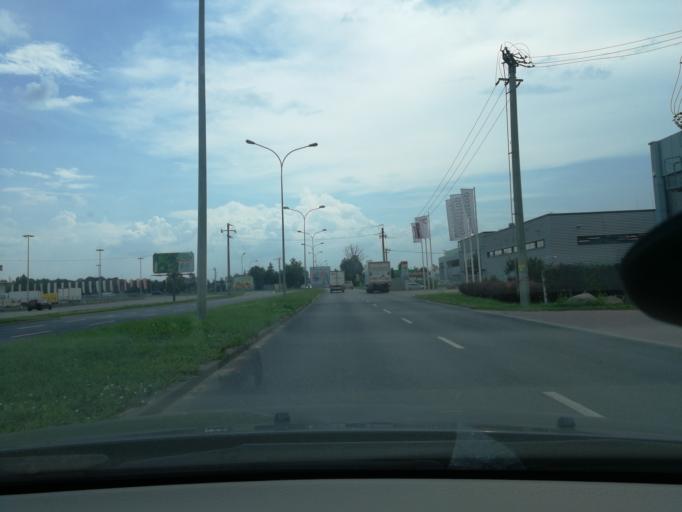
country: PL
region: Masovian Voivodeship
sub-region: Powiat pruszkowski
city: Piastow
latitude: 52.2172
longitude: 20.8387
